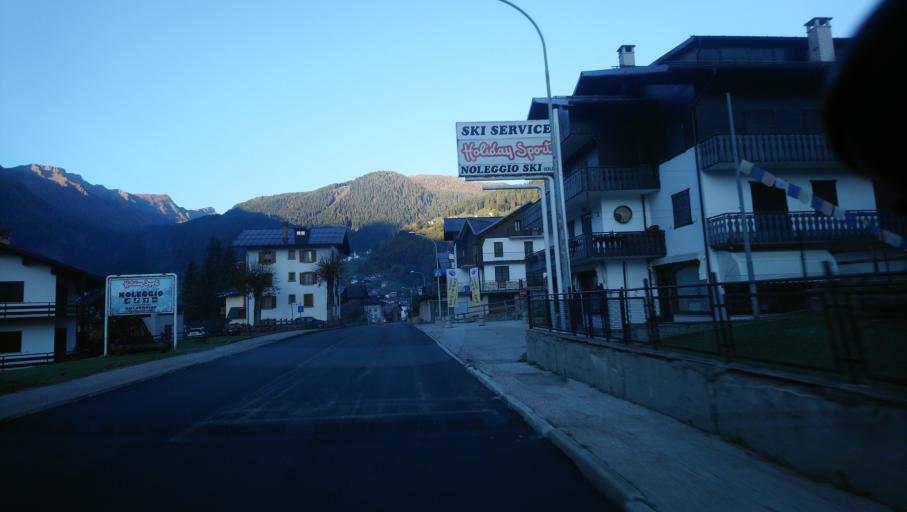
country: IT
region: Veneto
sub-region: Provincia di Belluno
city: Pie' Falcade
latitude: 46.3589
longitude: 11.8808
